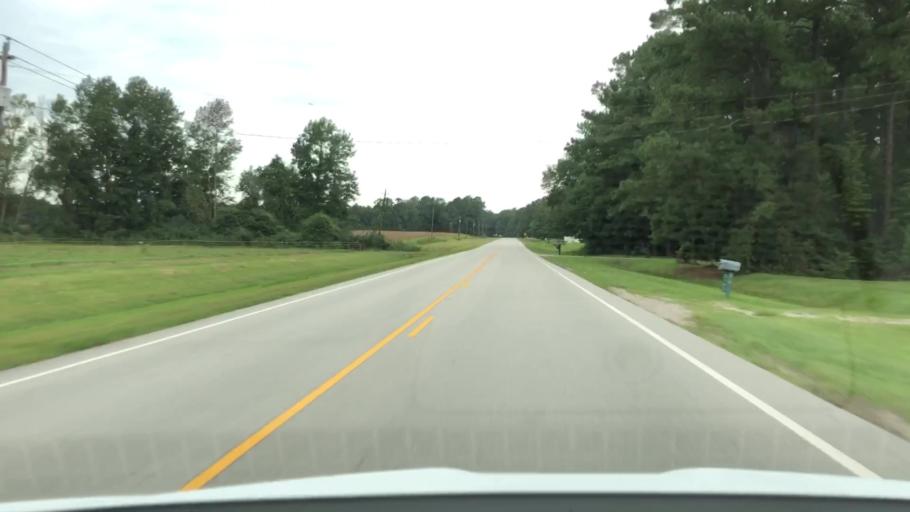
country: US
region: North Carolina
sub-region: Jones County
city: Trenton
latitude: 35.0290
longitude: -77.3111
